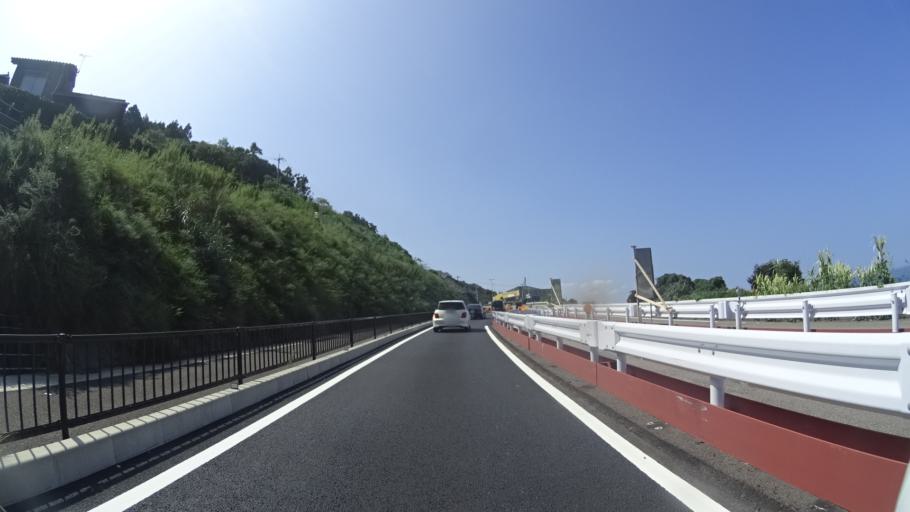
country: JP
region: Shimane
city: Masuda
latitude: 34.7407
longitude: 131.8755
